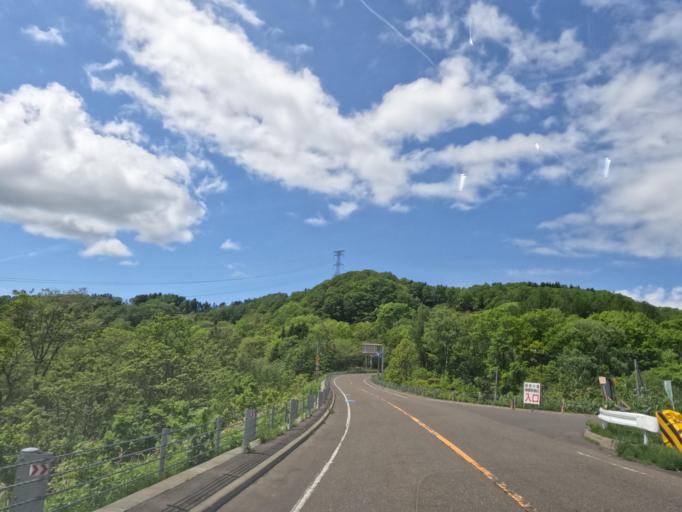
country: JP
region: Hokkaido
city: Sunagawa
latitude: 43.5026
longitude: 141.6073
